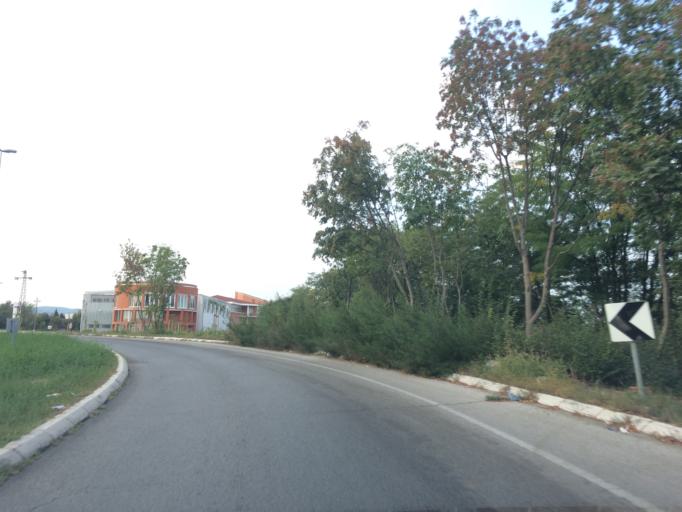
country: RS
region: Autonomna Pokrajina Vojvodina
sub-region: Juznobacki Okrug
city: Novi Sad
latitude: 45.2291
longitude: 19.8537
